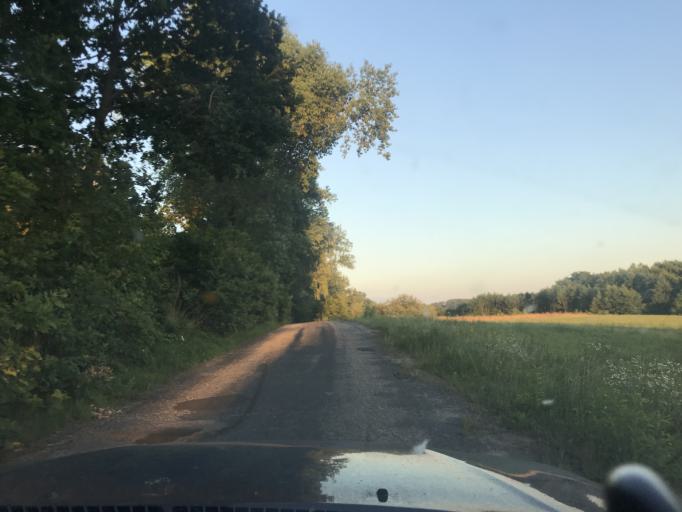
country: PL
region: West Pomeranian Voivodeship
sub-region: Powiat stargardzki
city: Chociwel
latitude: 53.4715
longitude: 15.3639
